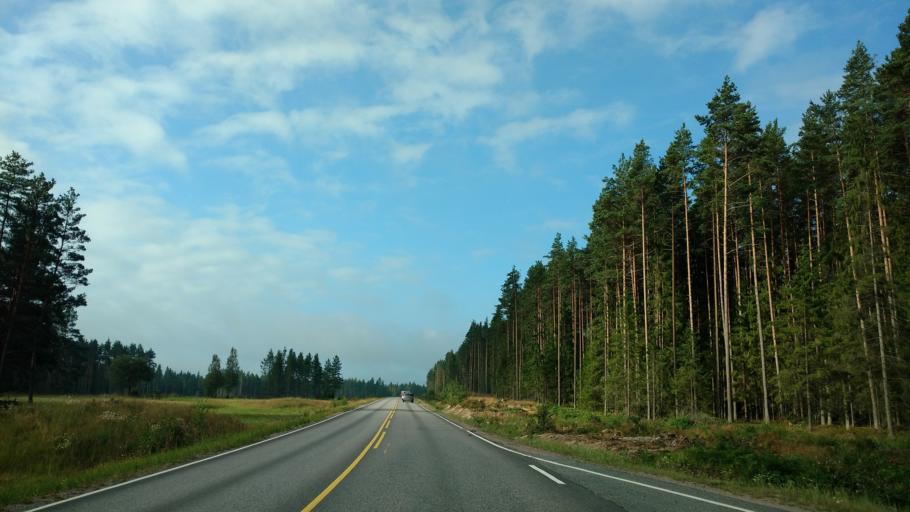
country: FI
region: Varsinais-Suomi
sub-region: Aboland-Turunmaa
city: Vaestanfjaerd
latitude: 60.1258
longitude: 22.6283
